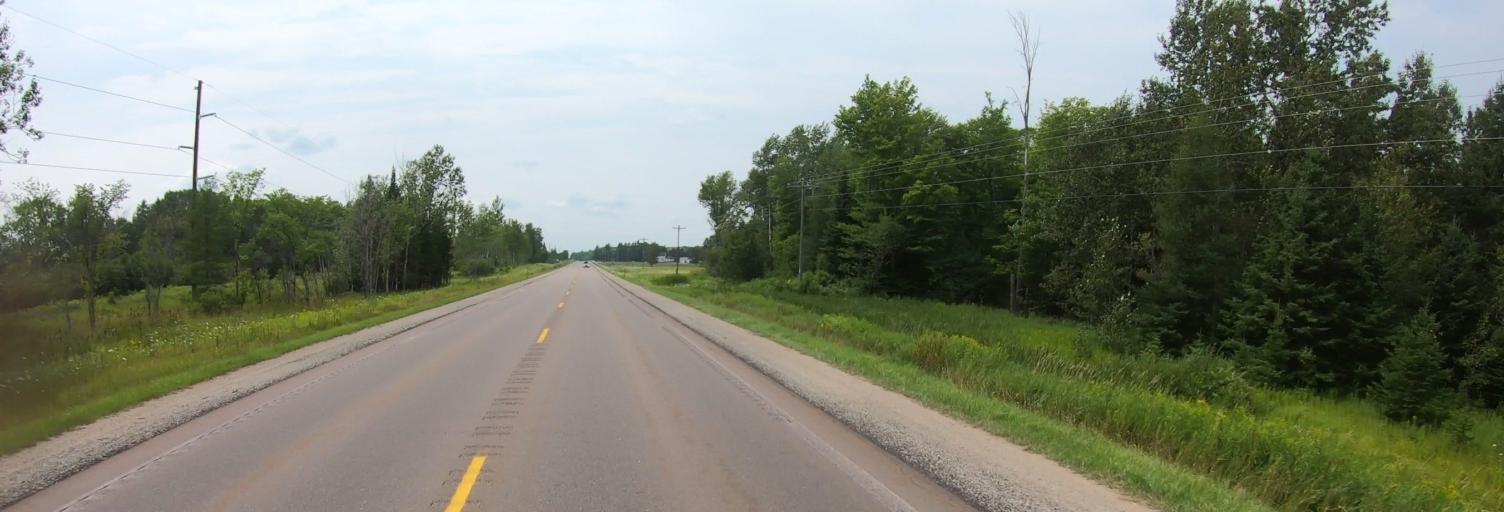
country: US
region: Michigan
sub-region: Marquette County
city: Harvey
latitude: 46.3509
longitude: -87.0195
